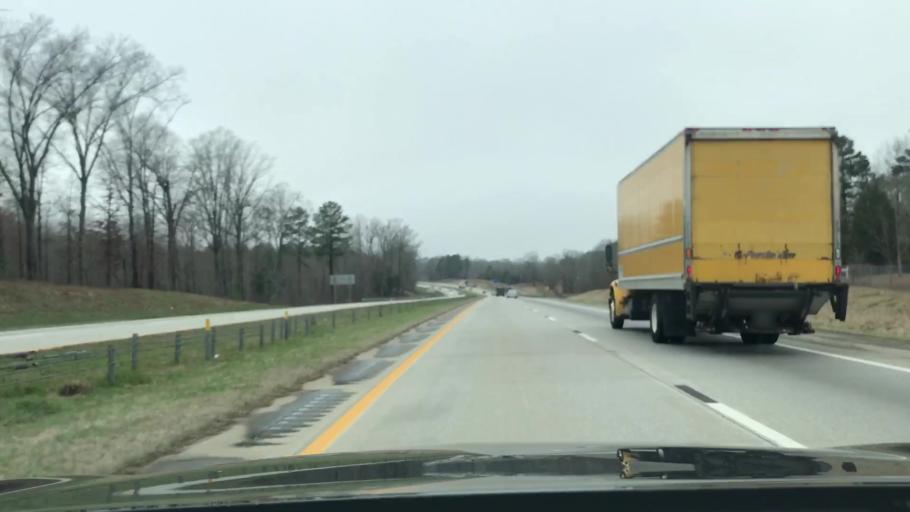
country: US
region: South Carolina
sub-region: Laurens County
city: Watts Mills
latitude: 34.5483
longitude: -81.9847
